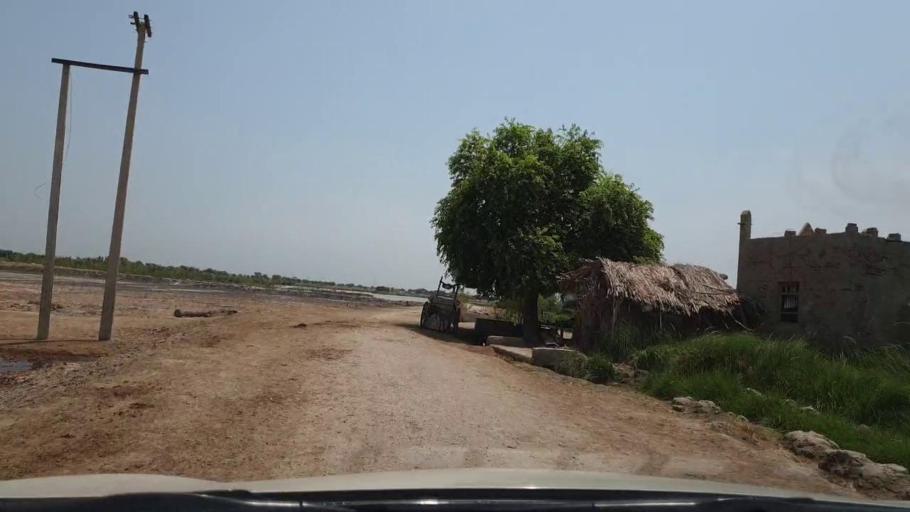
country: PK
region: Sindh
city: Ratodero
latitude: 27.8087
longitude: 68.2431
